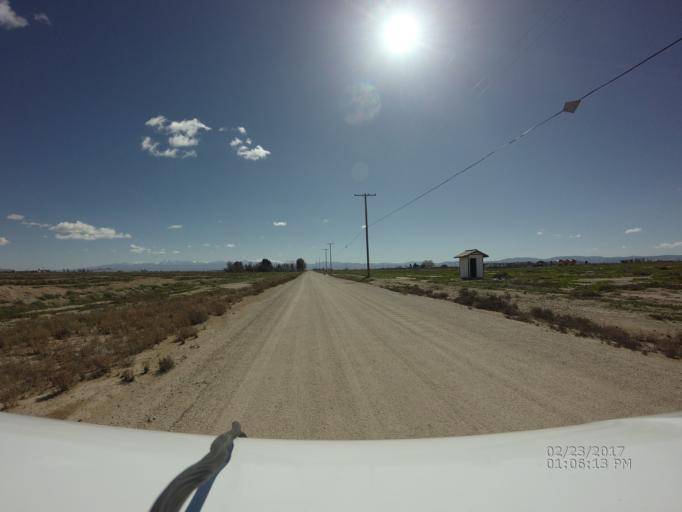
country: US
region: California
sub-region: Los Angeles County
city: Lancaster
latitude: 34.7535
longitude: -118.0144
